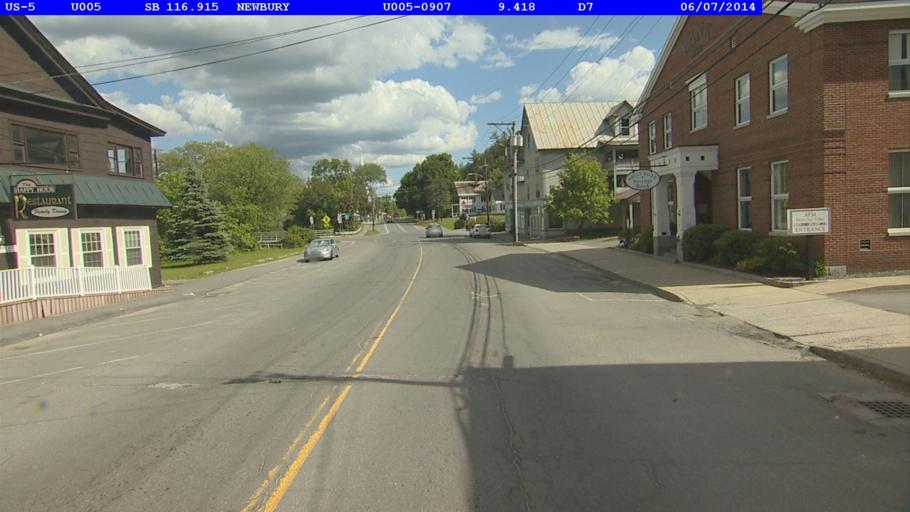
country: US
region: New Hampshire
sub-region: Grafton County
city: Woodsville
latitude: 44.1531
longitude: -72.0466
